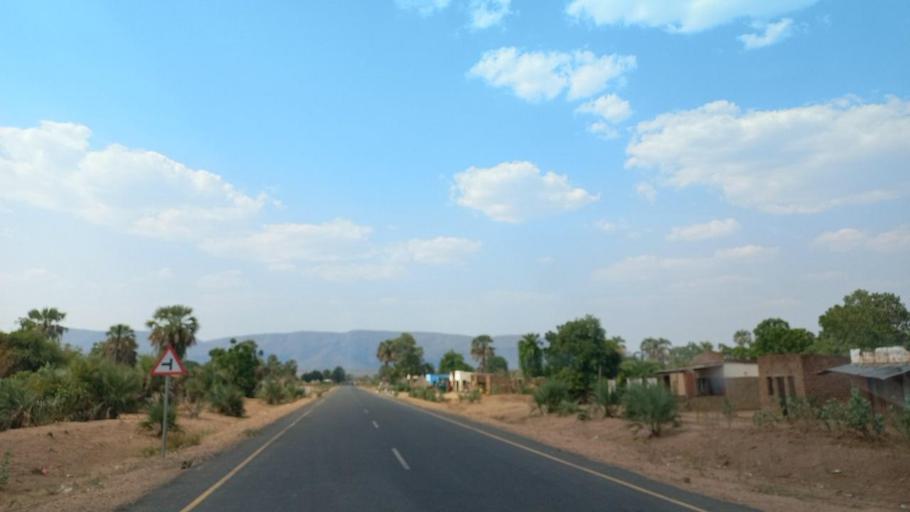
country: ZM
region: Lusaka
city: Luangwa
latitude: -15.0857
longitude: 30.1931
